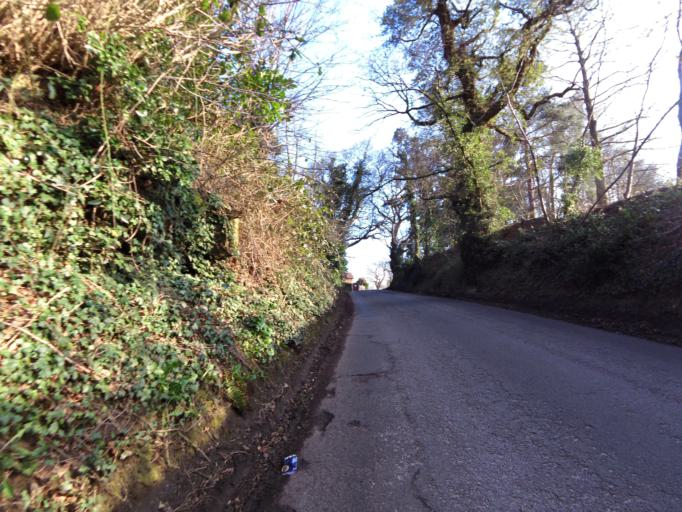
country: GB
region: England
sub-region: Suffolk
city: Kesgrave
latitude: 52.0779
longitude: 1.2531
